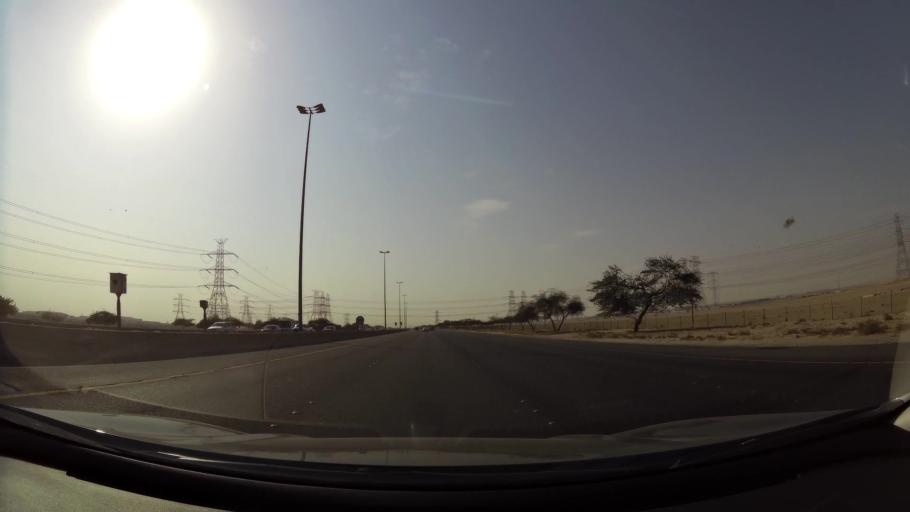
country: KW
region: Al Ahmadi
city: Al Ahmadi
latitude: 29.0159
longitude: 48.0924
